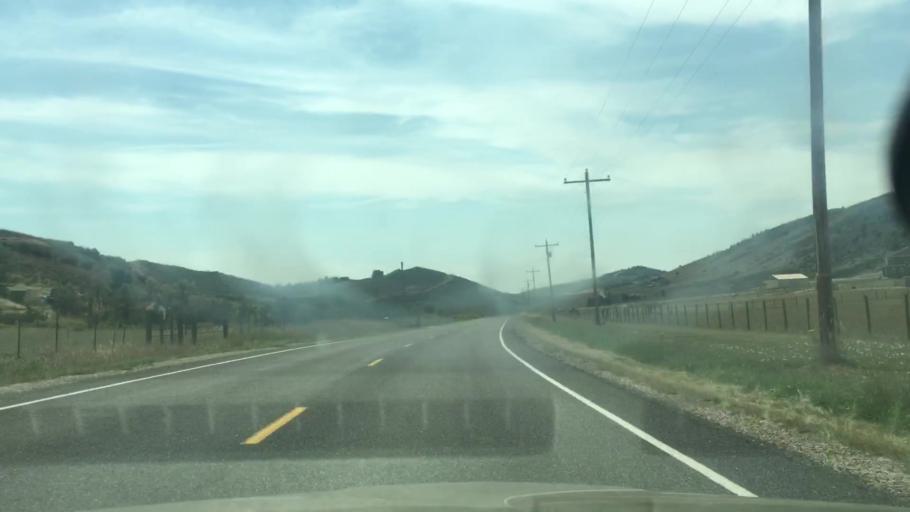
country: US
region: Colorado
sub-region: Larimer County
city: Campion
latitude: 40.3456
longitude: -105.1839
